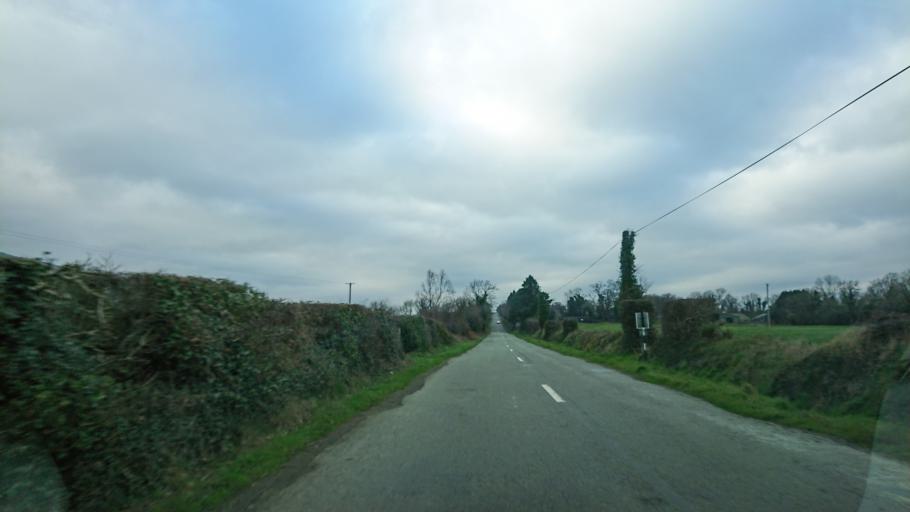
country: IE
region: Munster
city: Carrick-on-Suir
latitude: 52.3184
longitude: -7.5522
